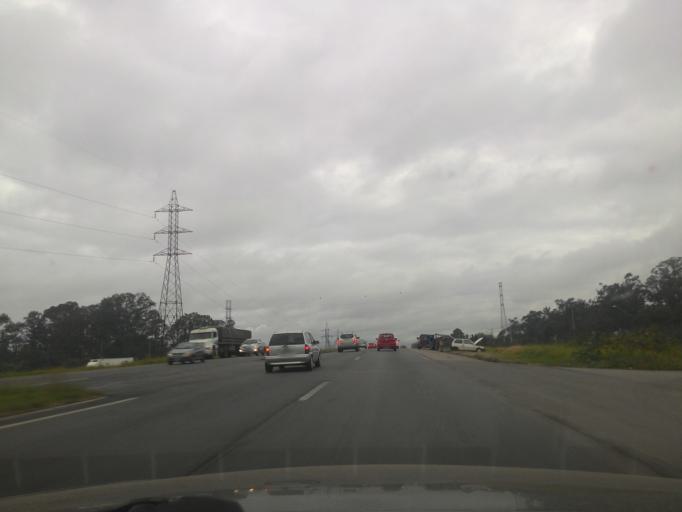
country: BR
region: Parana
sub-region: Araucaria
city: Araucaria
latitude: -25.5492
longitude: -49.3247
